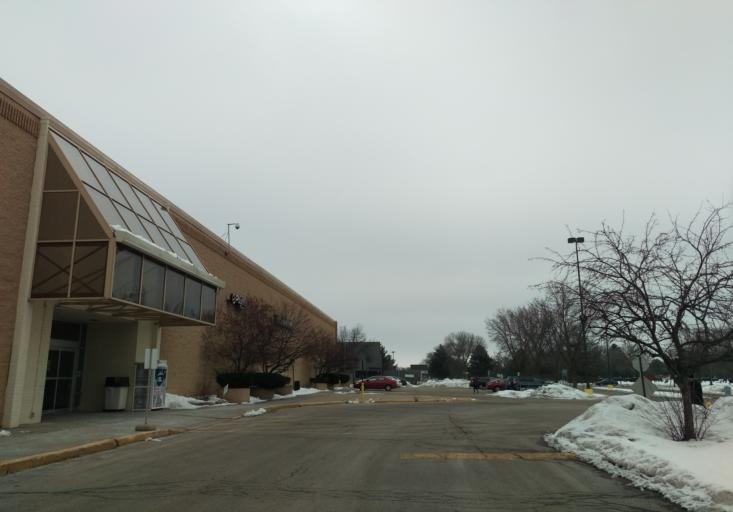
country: US
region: Wisconsin
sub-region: Dane County
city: Middleton
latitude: 43.0595
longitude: -89.5106
